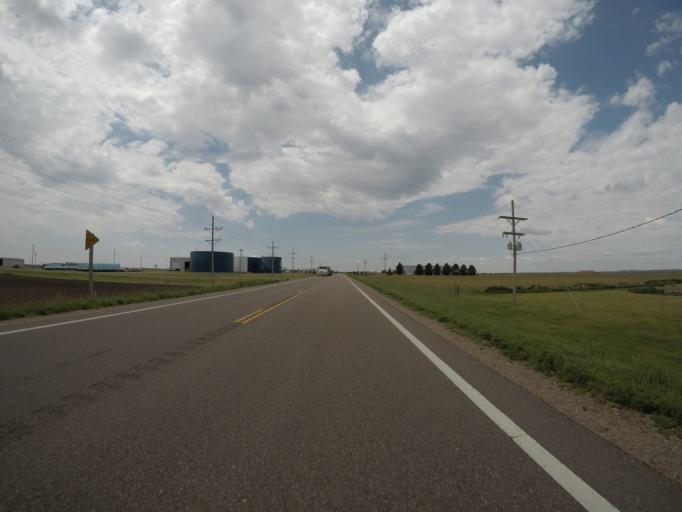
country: US
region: Kansas
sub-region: Thomas County
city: Colby
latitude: 39.3943
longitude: -101.0113
